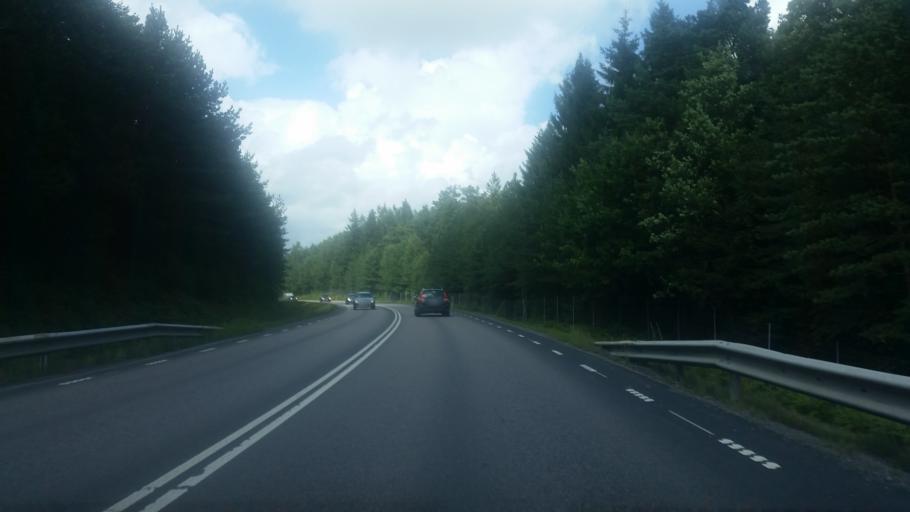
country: SE
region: Vaestra Goetaland
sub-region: Partille Kommun
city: Furulund
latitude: 57.7090
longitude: 12.1516
